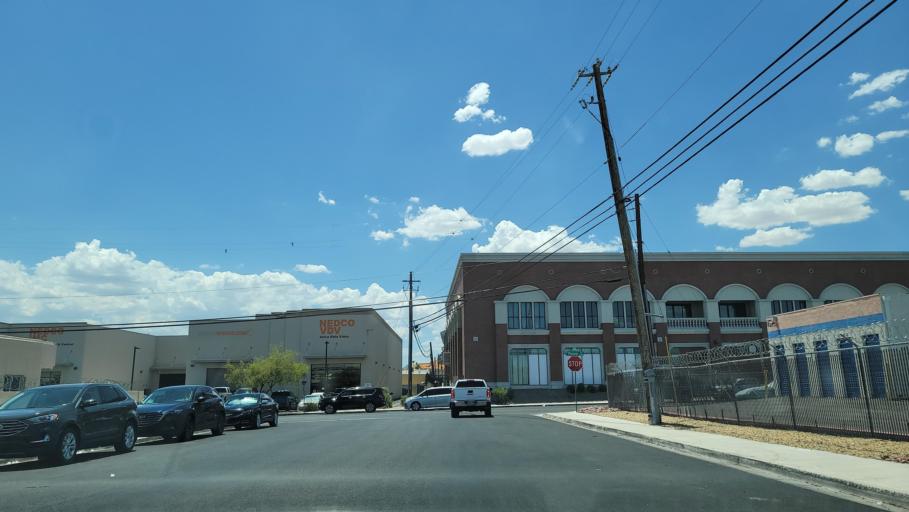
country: US
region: Nevada
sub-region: Clark County
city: Spring Valley
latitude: 36.1287
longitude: -115.1970
